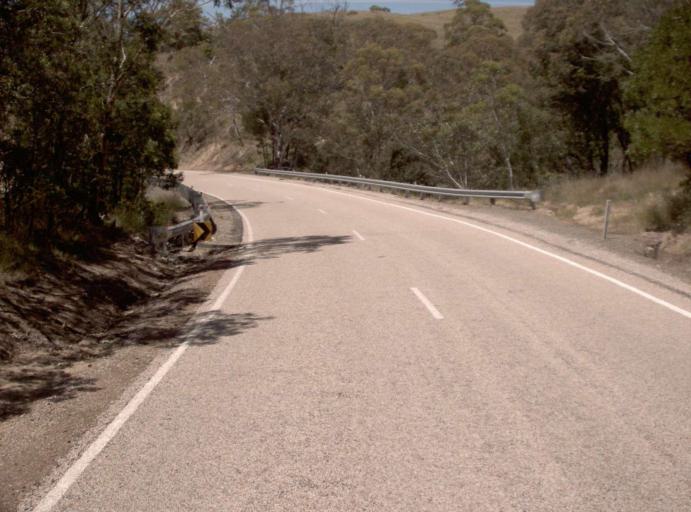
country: AU
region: Victoria
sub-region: Alpine
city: Mount Beauty
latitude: -37.1566
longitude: 147.6517
